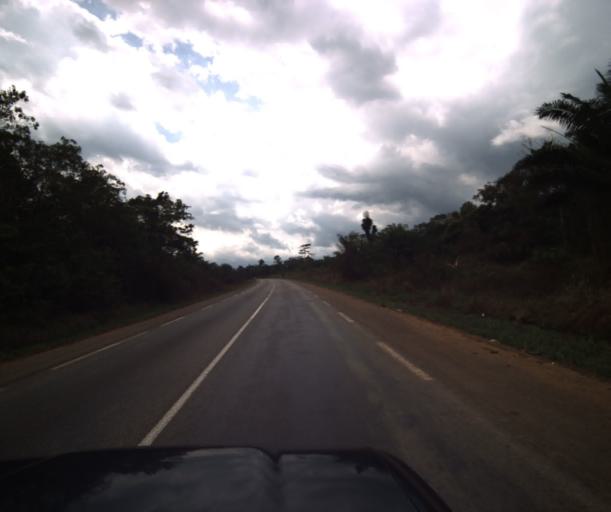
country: CM
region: Littoral
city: Edea
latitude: 3.8544
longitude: 10.0845
